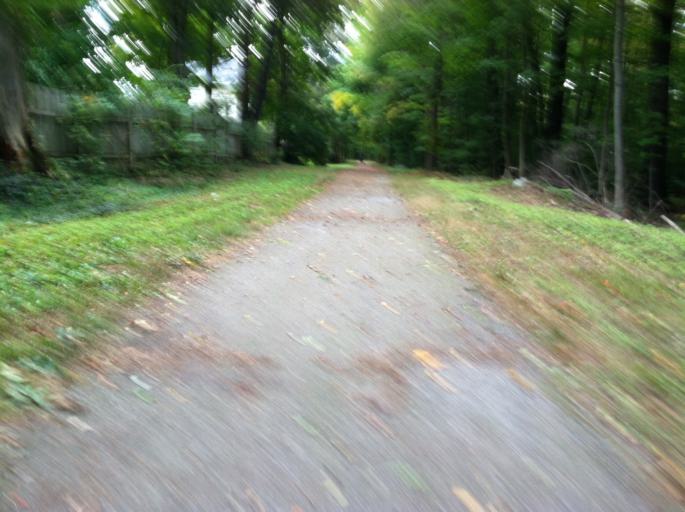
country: US
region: Massachusetts
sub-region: Middlesex County
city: Bedford
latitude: 42.4919
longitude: -71.2759
